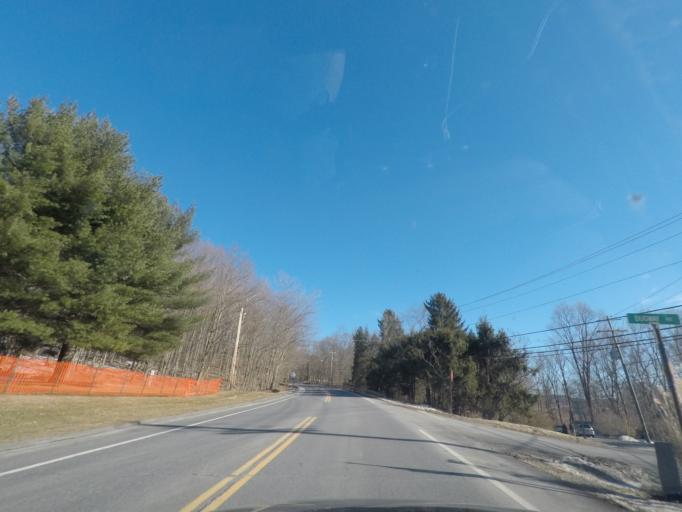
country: US
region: New York
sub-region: Columbia County
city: Chatham
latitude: 42.3212
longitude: -73.5425
